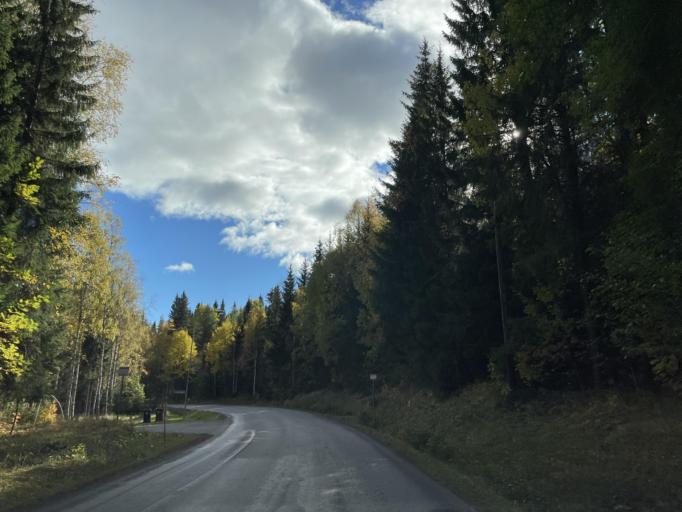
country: SE
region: Dalarna
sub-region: Malung-Saelens kommun
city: Malung
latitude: 61.1395
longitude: 13.2698
